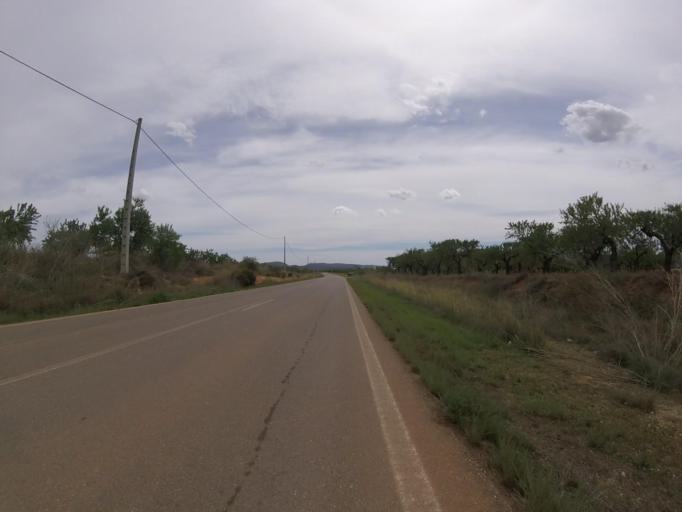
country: ES
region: Valencia
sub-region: Provincia de Castello
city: Cabanes
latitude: 40.1694
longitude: 0.0004
